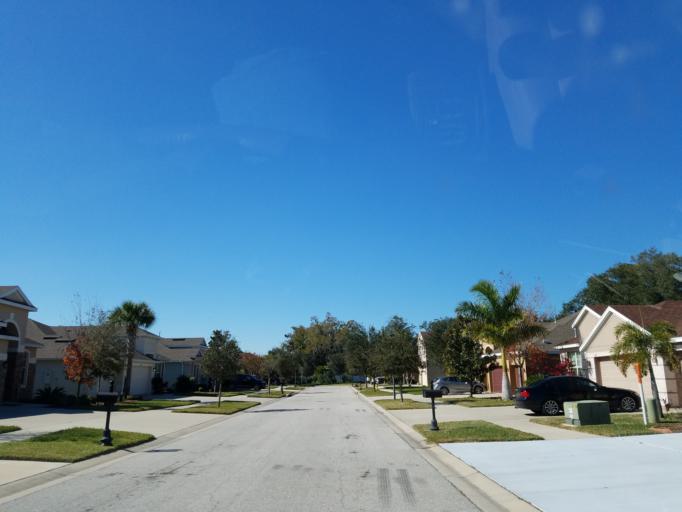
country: US
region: Florida
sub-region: Hillsborough County
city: Riverview
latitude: 27.8100
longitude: -82.3395
